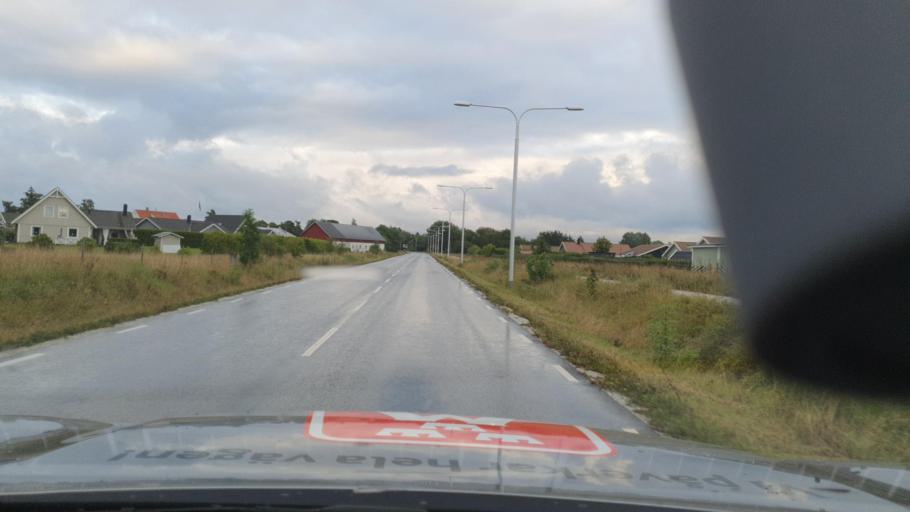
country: SE
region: Gotland
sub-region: Gotland
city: Vibble
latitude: 57.6058
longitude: 18.2360
